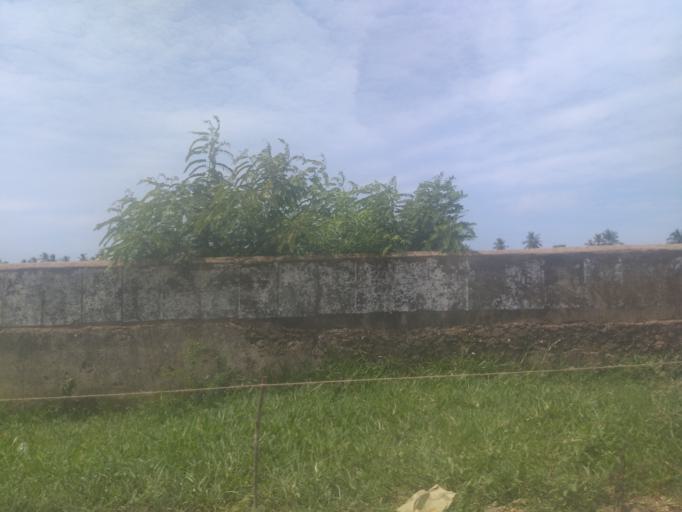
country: TZ
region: Zanzibar Urban/West
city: Zanzibar
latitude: -6.2154
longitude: 39.2118
